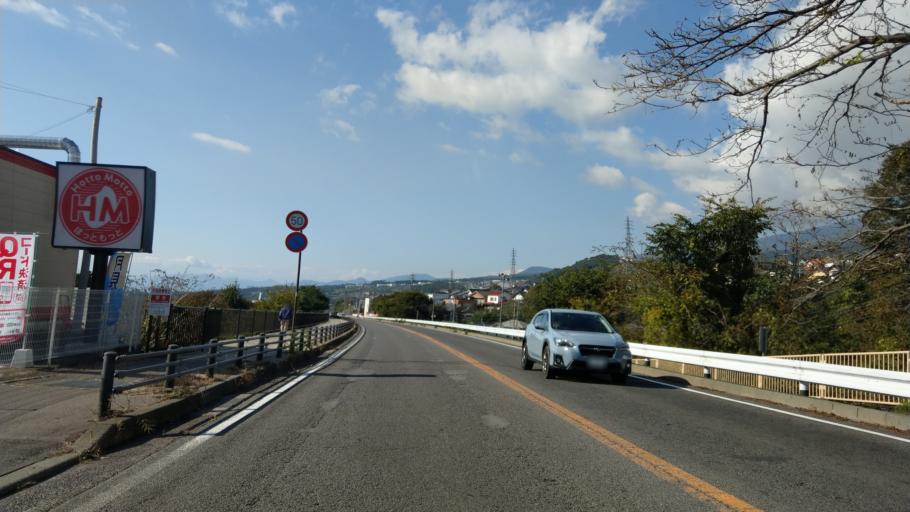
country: JP
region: Nagano
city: Komoro
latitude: 36.3318
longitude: 138.4301
